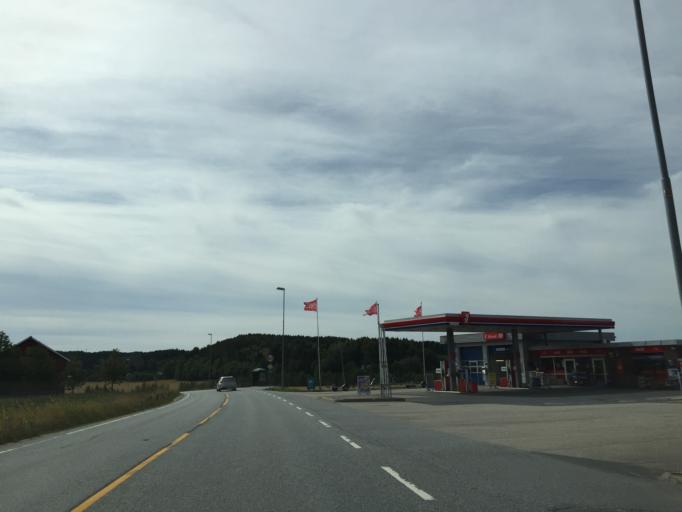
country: NO
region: Ostfold
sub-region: Fredrikstad
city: Fredrikstad
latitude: 59.2616
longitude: 10.8926
